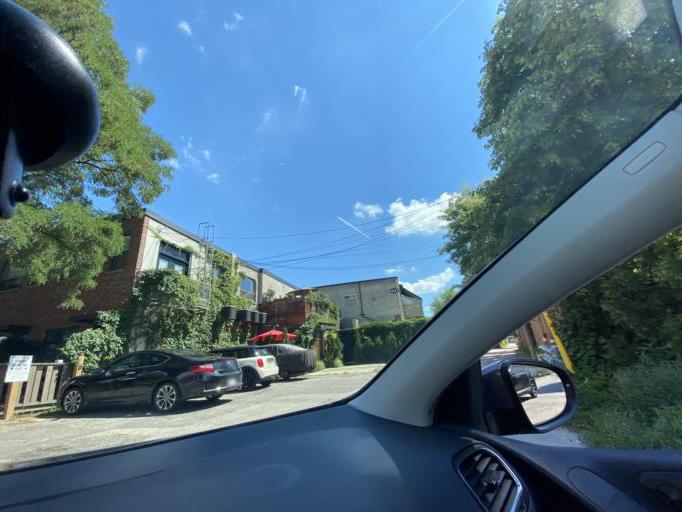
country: CA
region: Ontario
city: Etobicoke
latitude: 43.6652
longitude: -79.4949
